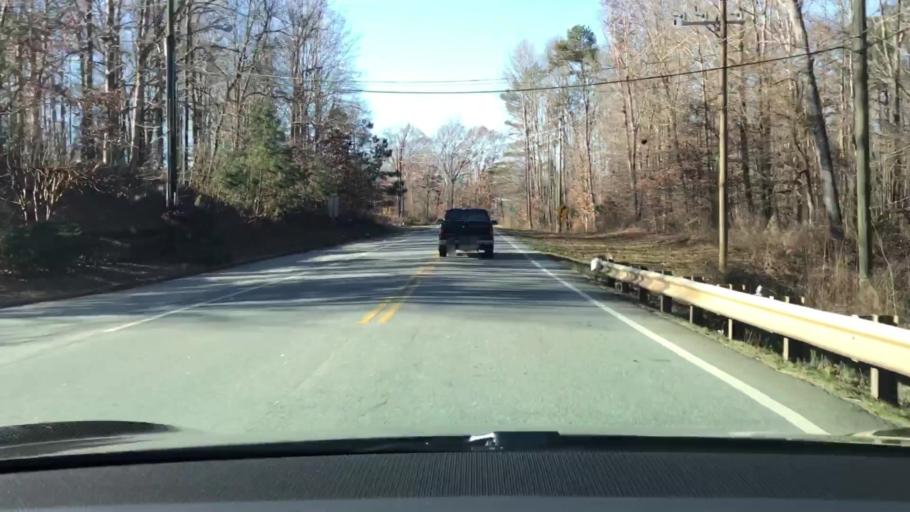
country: US
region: Georgia
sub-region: Barrow County
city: Auburn
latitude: 34.0995
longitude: -83.8691
